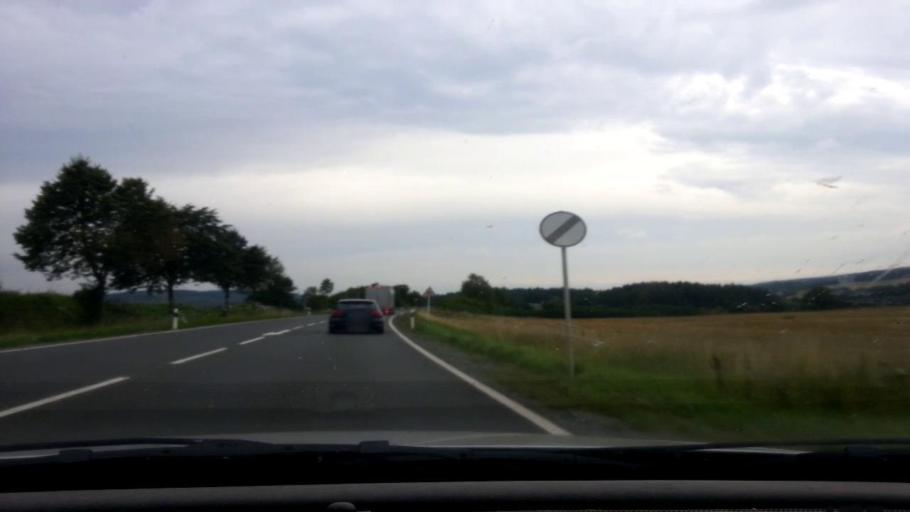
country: DE
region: Bavaria
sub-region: Upper Franconia
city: Seybothenreuth
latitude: 49.8992
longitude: 11.7002
